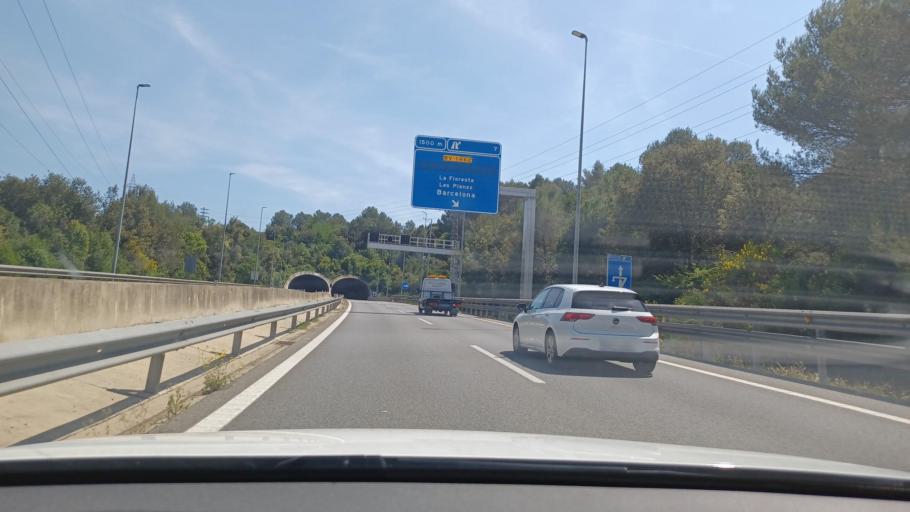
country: ES
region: Catalonia
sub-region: Provincia de Barcelona
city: Sant Cugat del Valles
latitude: 41.4552
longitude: 2.0675
